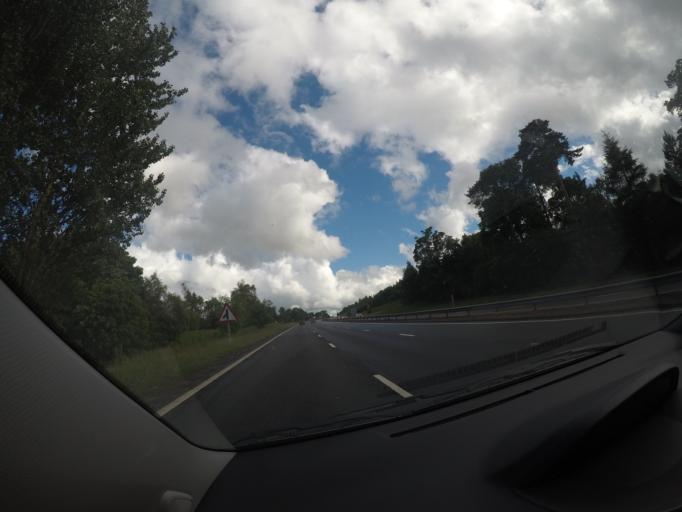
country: GB
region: Scotland
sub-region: South Lanarkshire
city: Douglas
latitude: 55.5741
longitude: -3.8124
